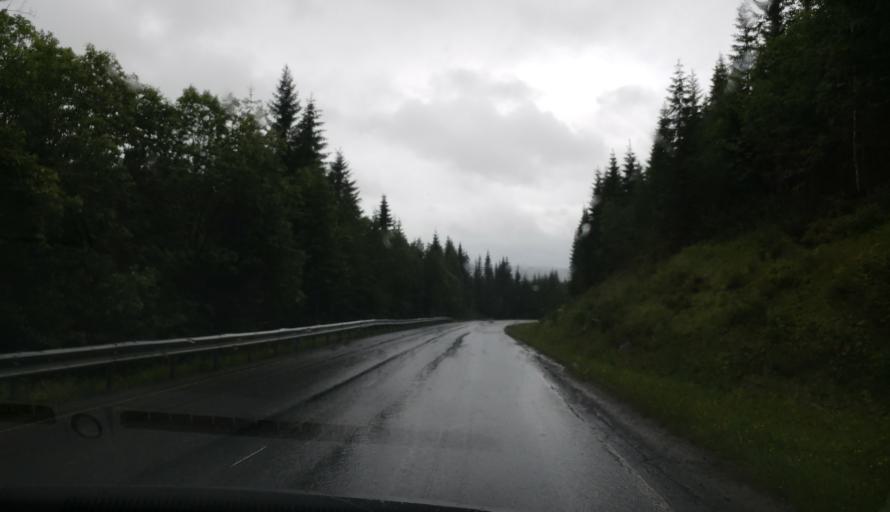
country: NO
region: Sor-Trondelag
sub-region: Selbu
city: Mebonden
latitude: 63.3020
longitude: 11.0785
